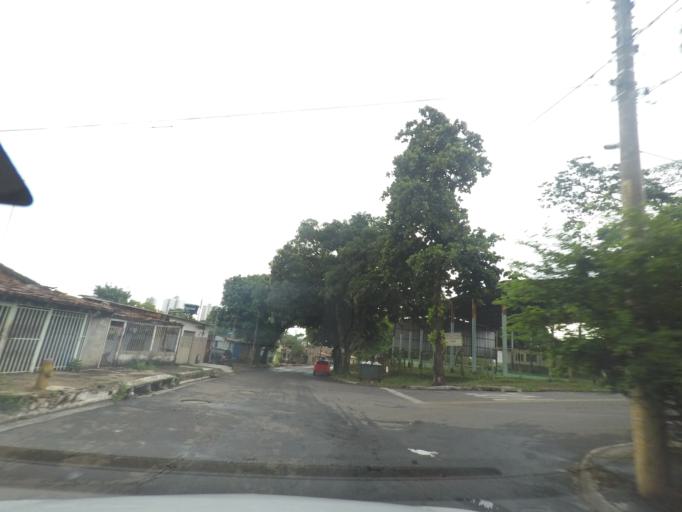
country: BR
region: Goias
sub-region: Goiania
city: Goiania
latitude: -16.7206
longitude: -49.2454
